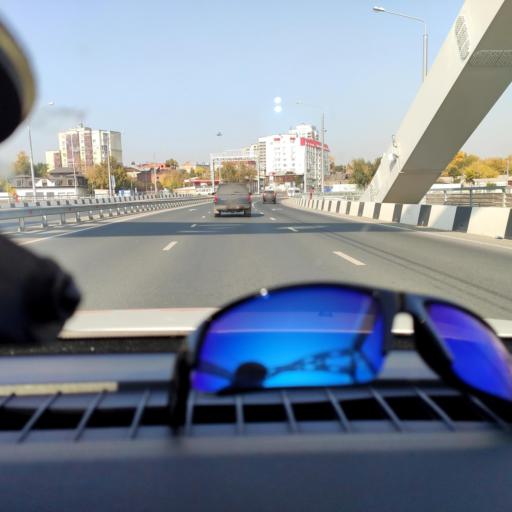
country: RU
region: Samara
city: Rozhdestveno
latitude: 53.1771
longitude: 50.0856
